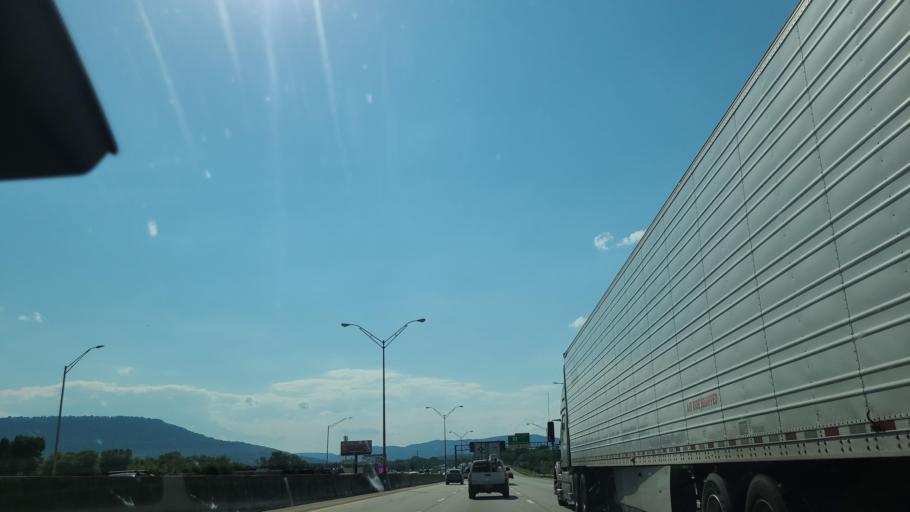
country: US
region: Tennessee
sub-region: Hamilton County
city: East Ridge
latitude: 35.0172
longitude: -85.2821
